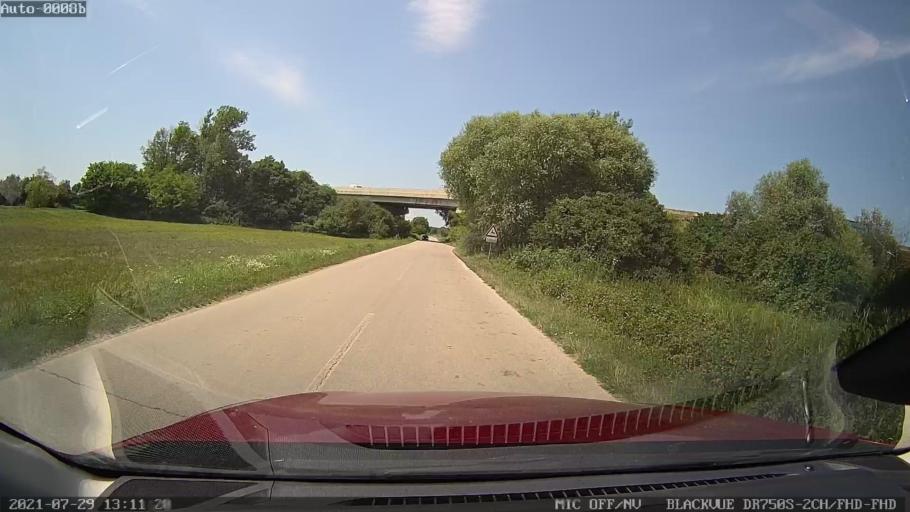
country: HR
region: Varazdinska
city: Jalzabet
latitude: 46.2773
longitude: 16.4322
